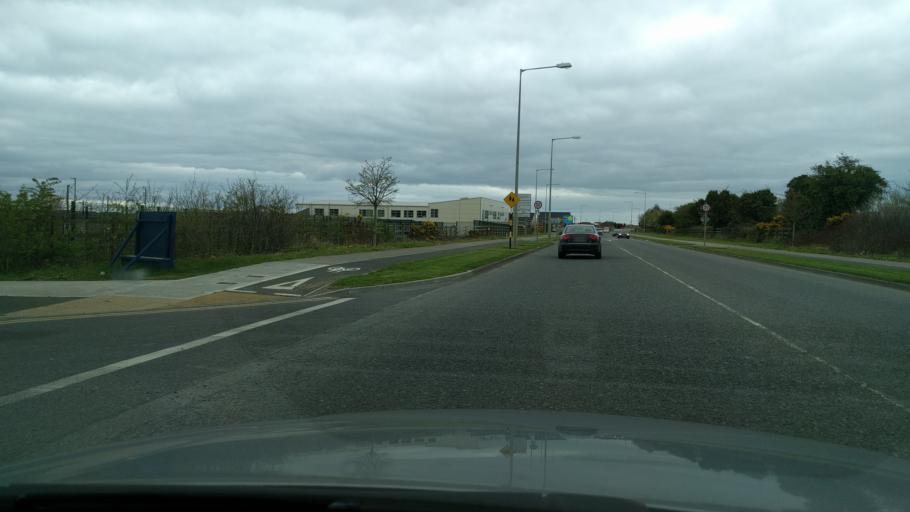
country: IE
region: Leinster
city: Balbriggan
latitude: 53.6060
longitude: -6.2058
